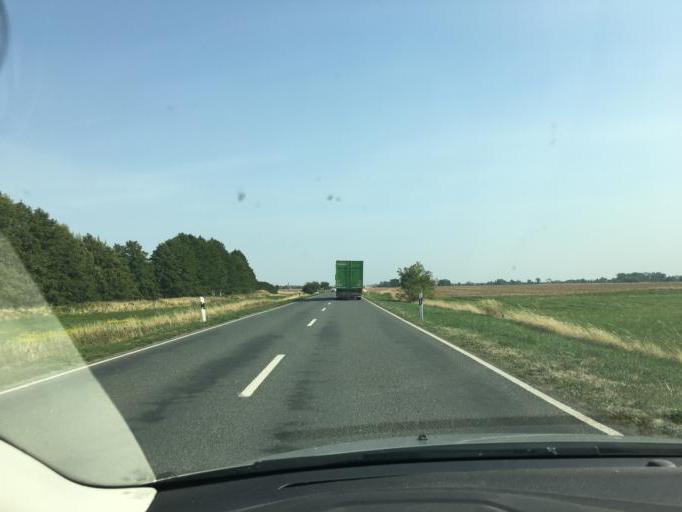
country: DE
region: Saxony-Anhalt
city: Plotzky
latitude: 52.0051
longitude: 11.8043
